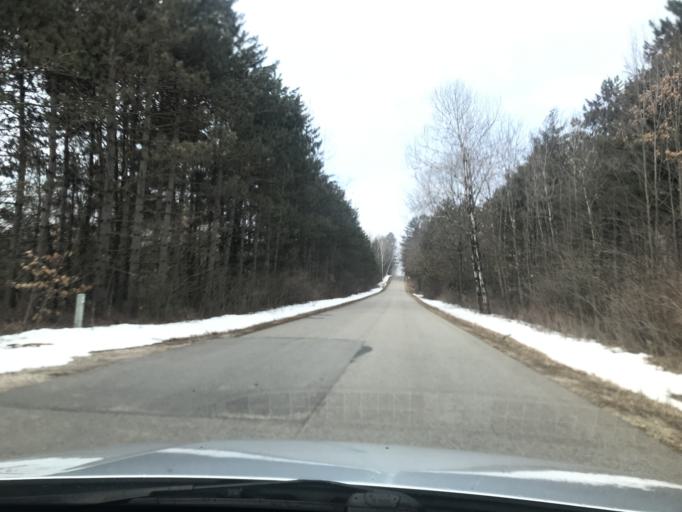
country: US
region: Wisconsin
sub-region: Oconto County
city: Oconto Falls
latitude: 44.8296
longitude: -88.1781
